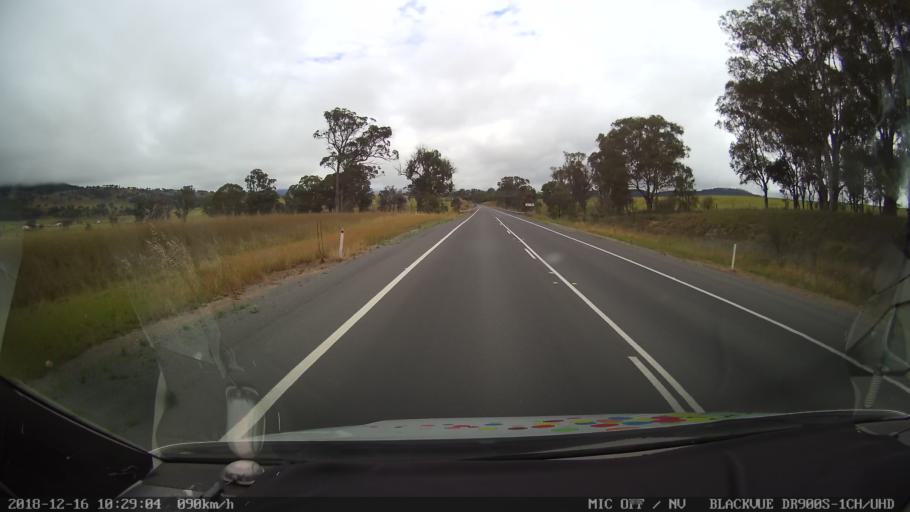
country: AU
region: New South Wales
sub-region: Tenterfield Municipality
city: Carrolls Creek
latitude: -29.1130
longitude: 151.9967
